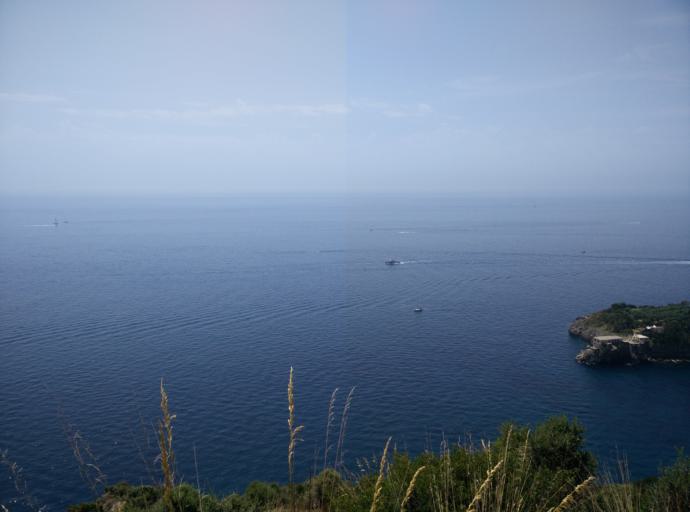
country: IT
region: Campania
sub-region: Provincia di Napoli
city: Massa Lubrense
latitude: 40.5936
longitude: 14.3796
